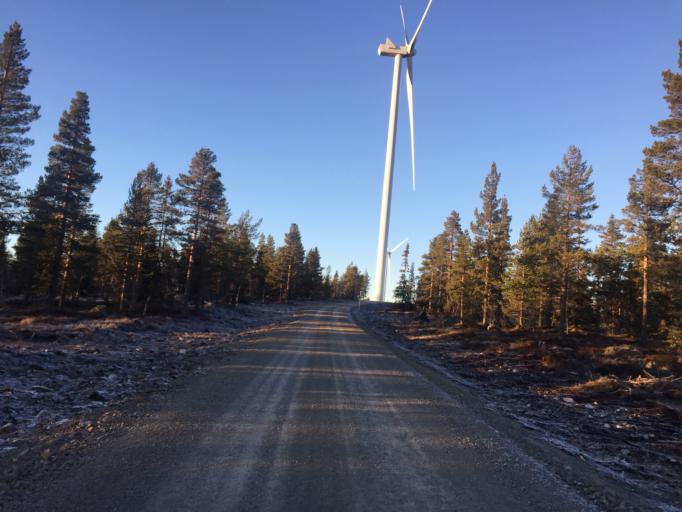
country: NO
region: Hedmark
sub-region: Elverum
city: Elverum
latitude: 61.2065
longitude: 11.7896
